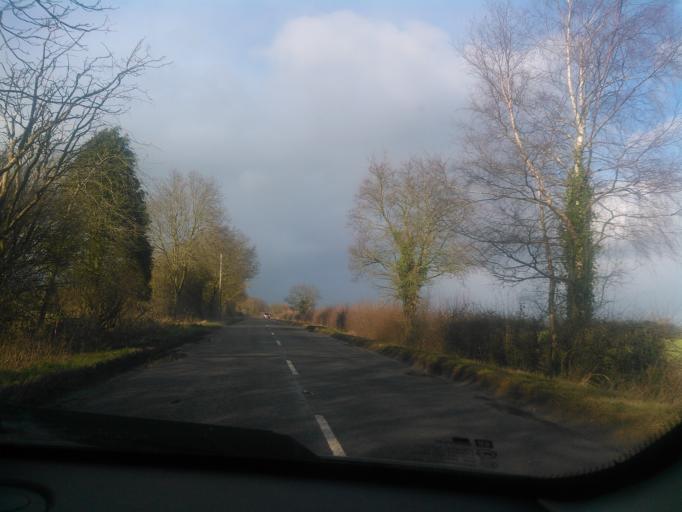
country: GB
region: England
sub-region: Shropshire
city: Shawbury
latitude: 52.7729
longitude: -2.6357
